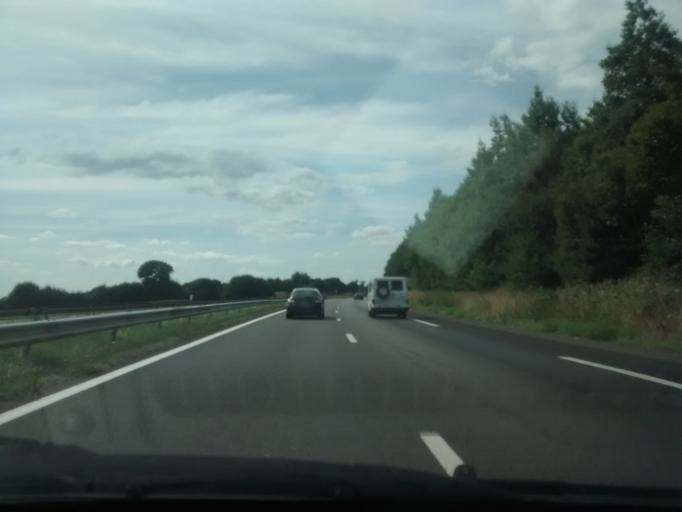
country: FR
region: Brittany
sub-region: Departement d'Ille-et-Vilaine
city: Montauban-de-Bretagne
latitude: 48.1896
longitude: -2.0163
